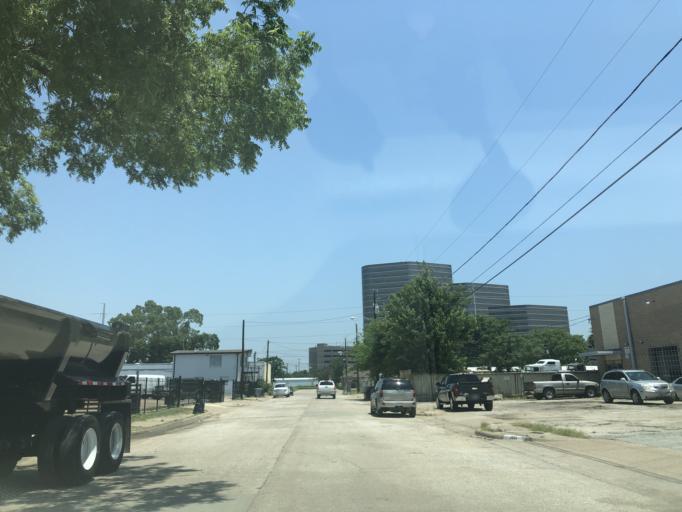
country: US
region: Texas
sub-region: Dallas County
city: Dallas
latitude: 32.8062
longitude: -96.8502
